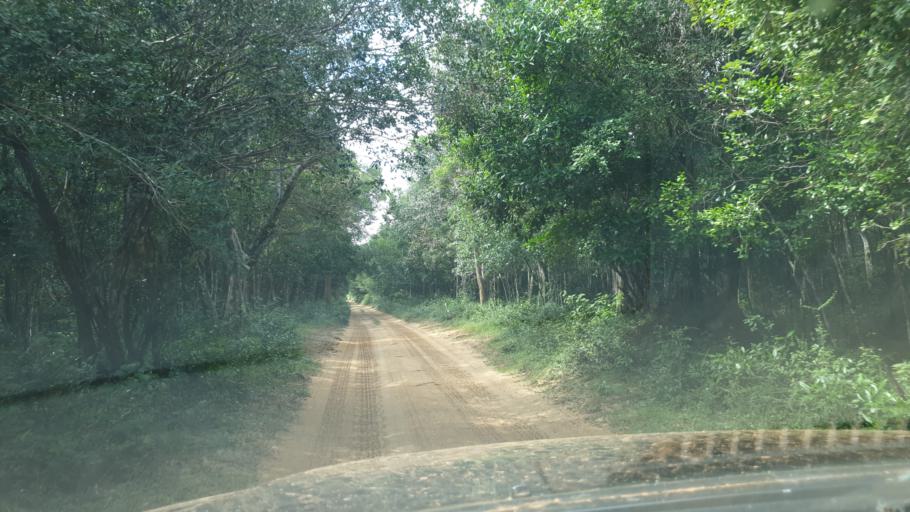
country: LK
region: North Central
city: Anuradhapura
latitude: 8.4189
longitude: 80.0178
